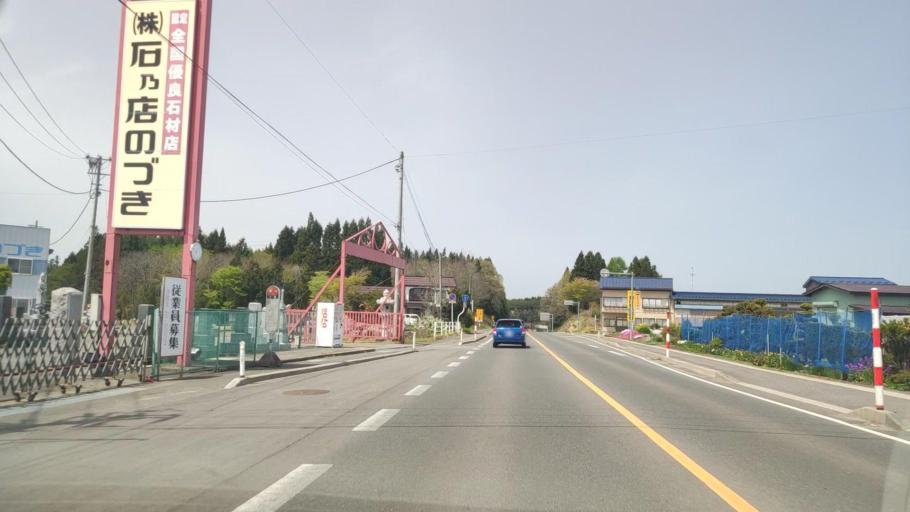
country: JP
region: Aomori
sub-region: Misawa Shi
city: Inuotose
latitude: 40.6595
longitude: 141.1912
